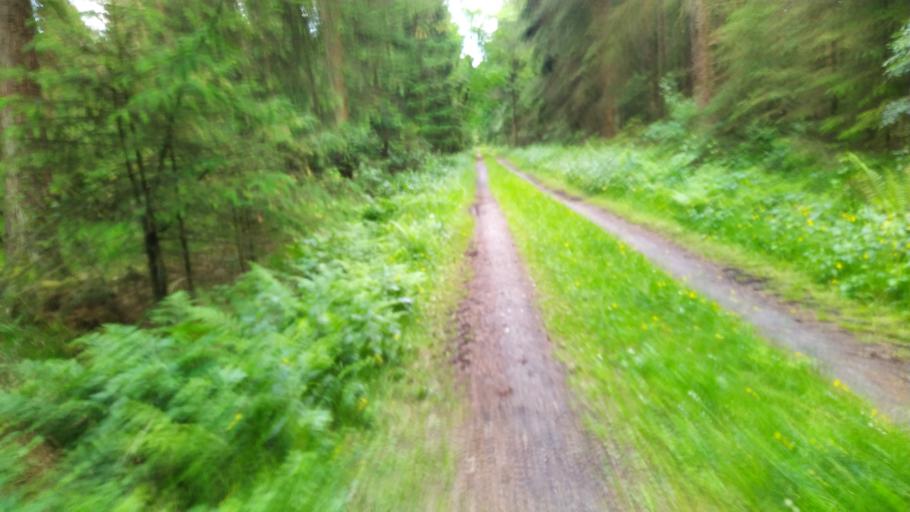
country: DE
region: Lower Saxony
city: Deinstedt
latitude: 53.4409
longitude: 9.2468
